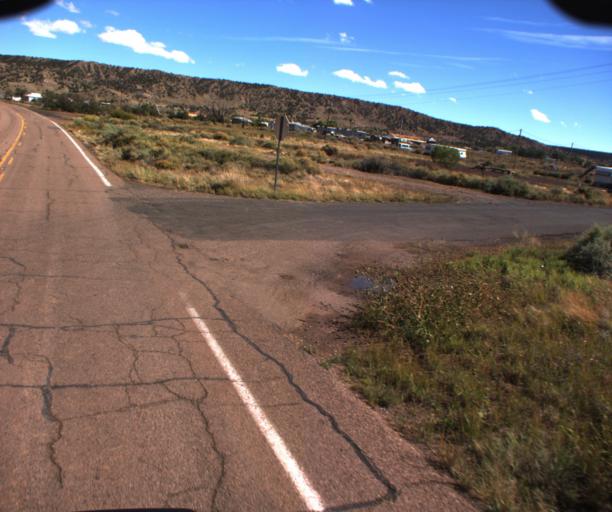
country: US
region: Arizona
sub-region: Apache County
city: Saint Johns
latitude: 34.4784
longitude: -109.6126
